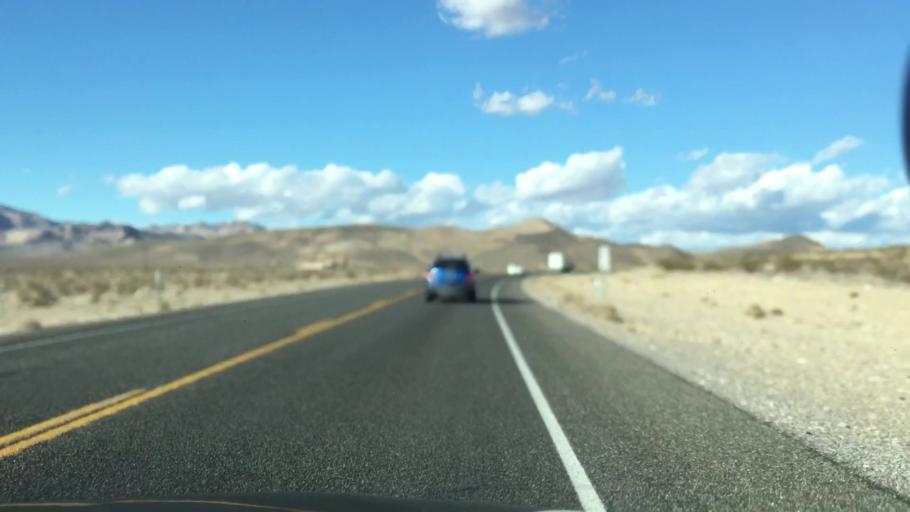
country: US
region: Nevada
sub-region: Nye County
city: Beatty
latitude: 36.8560
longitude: -116.7572
